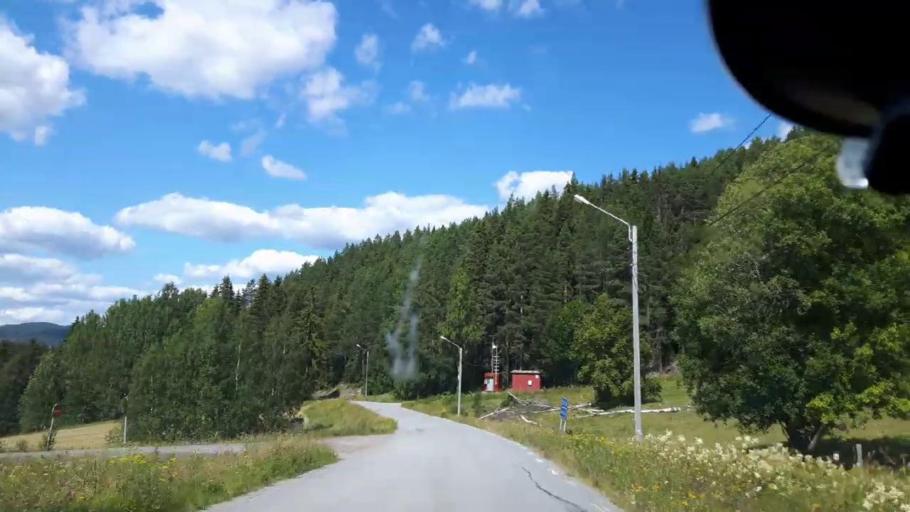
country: SE
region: Jaemtland
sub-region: Ragunda Kommun
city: Hammarstrand
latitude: 62.9553
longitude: 16.6832
